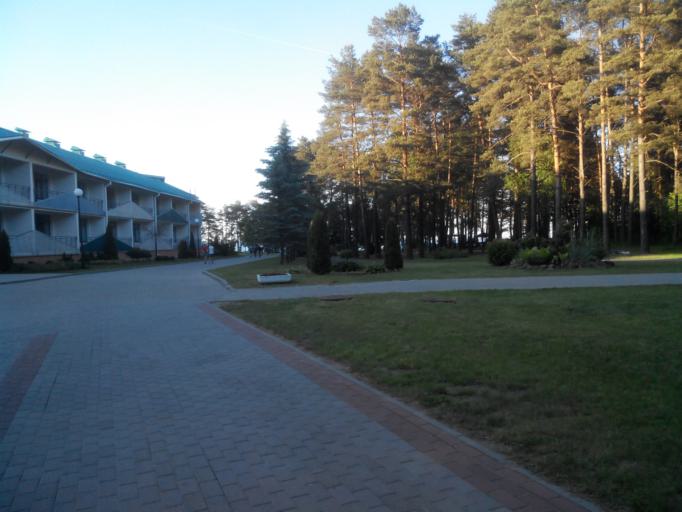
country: BY
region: Minsk
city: Narach
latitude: 54.8362
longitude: 26.7141
